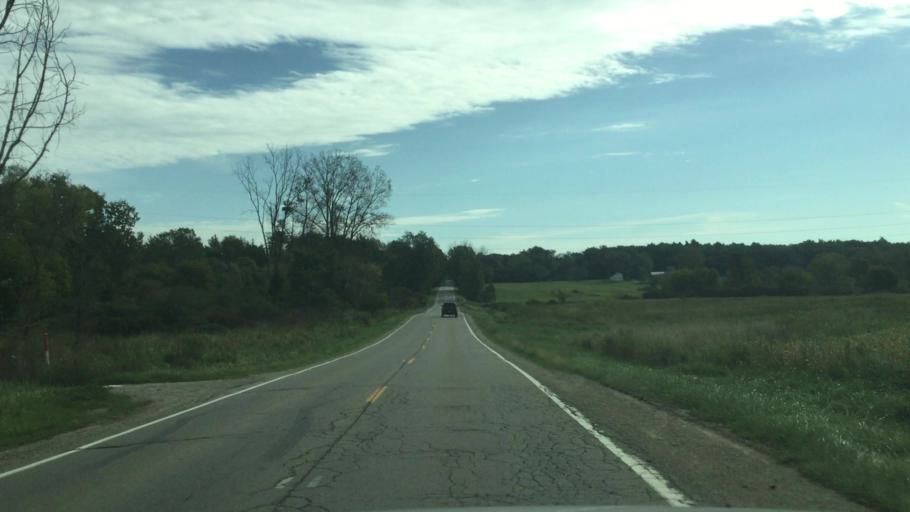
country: US
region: Michigan
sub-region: Genesee County
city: Argentine
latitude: 42.7038
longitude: -83.8785
